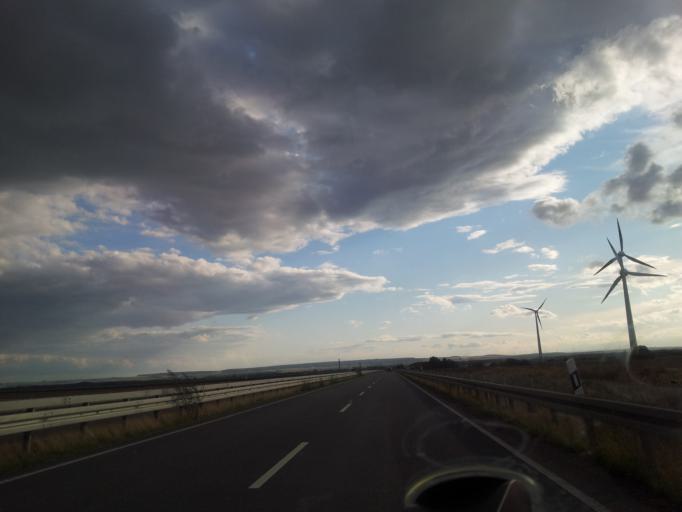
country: DE
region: Saxony-Anhalt
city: Wolmirsleben
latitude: 51.9726
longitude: 11.4644
